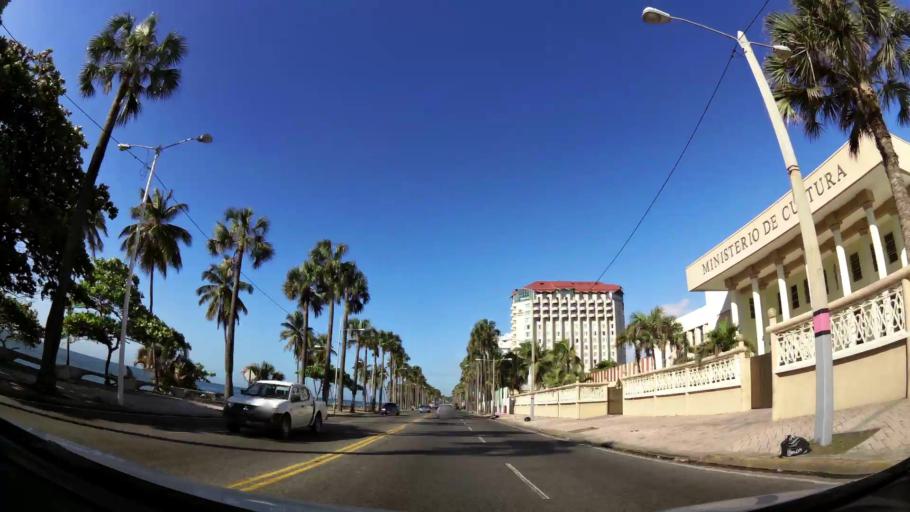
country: DO
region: Nacional
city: Ciudad Nueva
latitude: 18.4643
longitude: -69.8945
